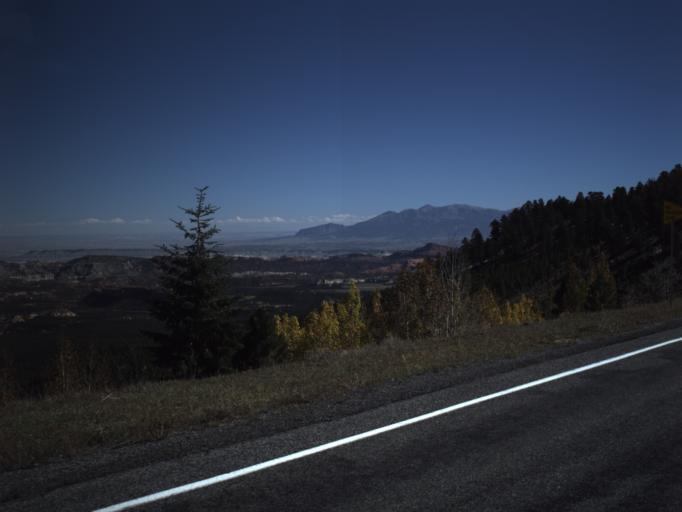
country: US
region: Utah
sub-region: Wayne County
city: Loa
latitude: 38.1213
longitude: -111.3286
